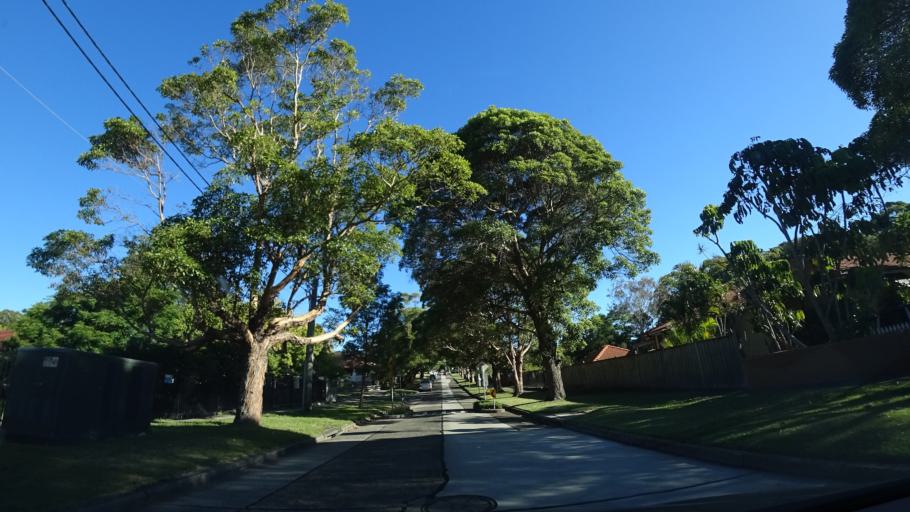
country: AU
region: New South Wales
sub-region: Willoughby
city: Chatswood
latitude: -33.7905
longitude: 151.1908
